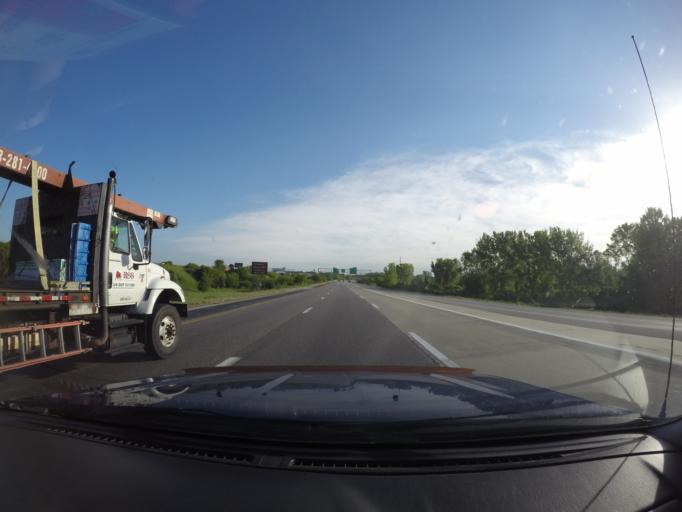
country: US
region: Missouri
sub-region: Platte County
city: Riverside
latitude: 39.1641
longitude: -94.6261
